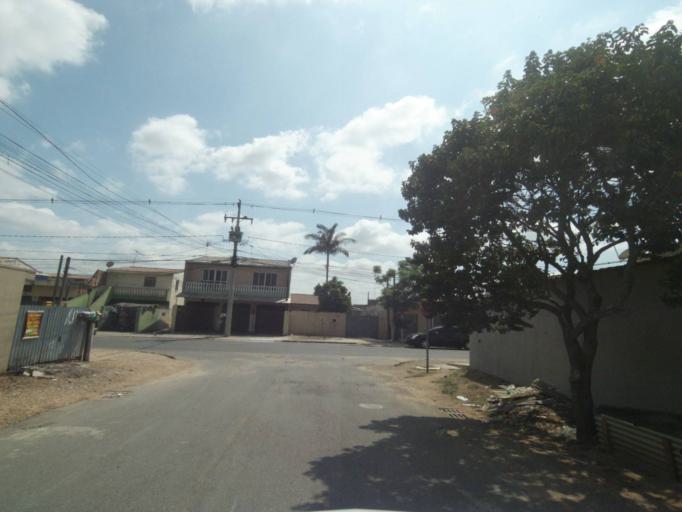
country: BR
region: Parana
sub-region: Sao Jose Dos Pinhais
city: Sao Jose dos Pinhais
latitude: -25.5411
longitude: -49.2608
